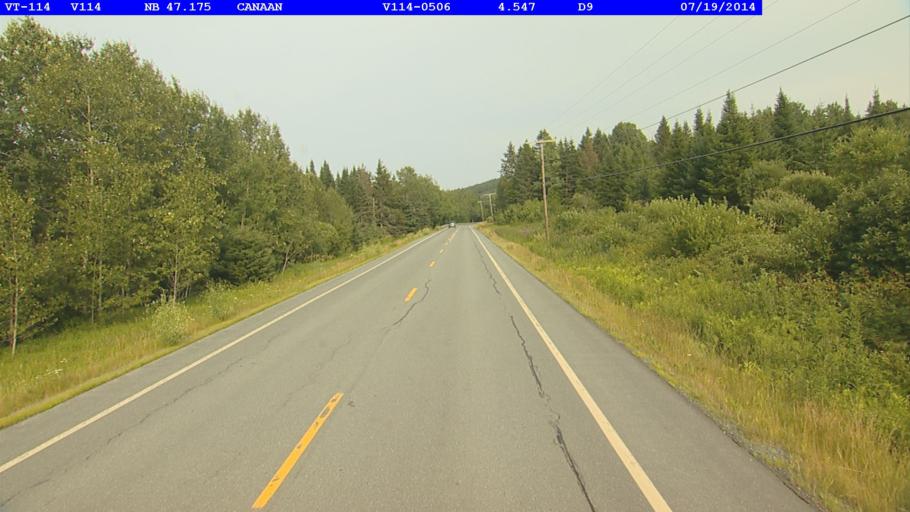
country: US
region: New Hampshire
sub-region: Coos County
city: Colebrook
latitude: 45.0073
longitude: -71.6034
